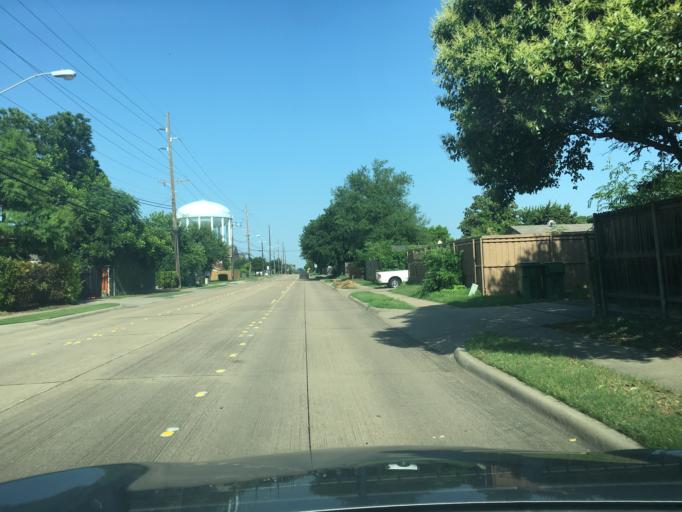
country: US
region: Texas
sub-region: Dallas County
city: Richardson
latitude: 32.9239
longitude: -96.6869
